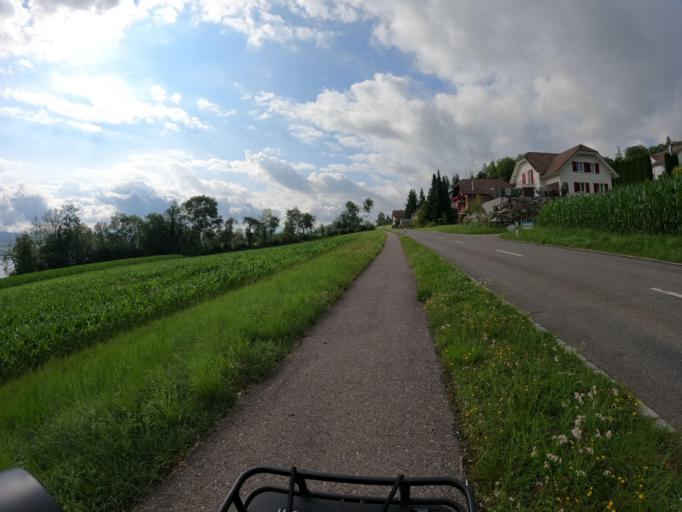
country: CH
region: Lucerne
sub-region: Hochdorf District
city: Hitzkirch
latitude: 47.2041
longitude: 8.2454
